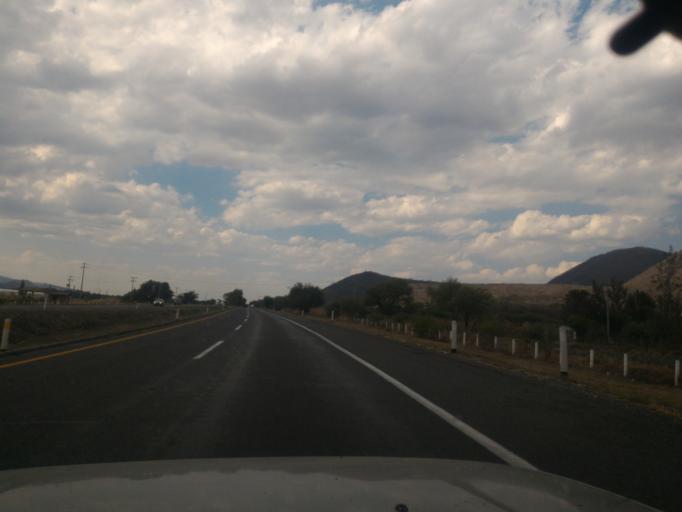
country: MX
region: Jalisco
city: Zacoalco de Torres
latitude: 20.1828
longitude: -103.5131
